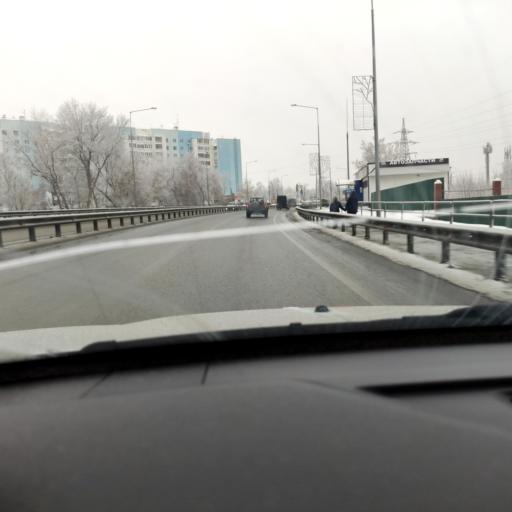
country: RU
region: Samara
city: Volzhskiy
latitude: 53.3521
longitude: 50.2154
